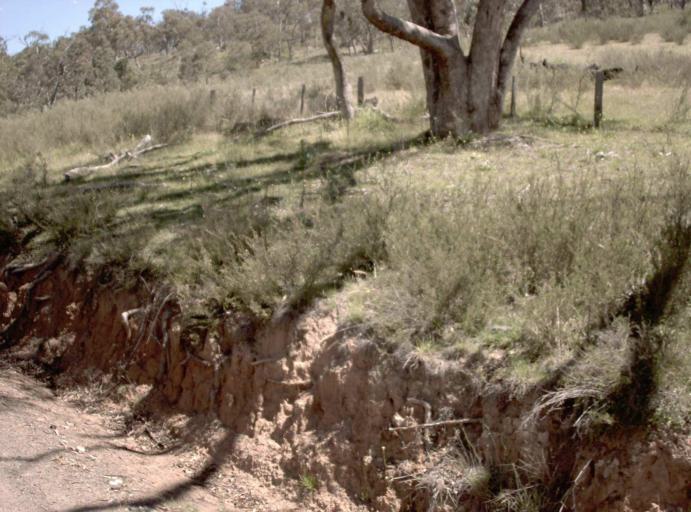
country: AU
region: New South Wales
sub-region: Snowy River
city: Jindabyne
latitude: -37.0495
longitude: 148.5632
